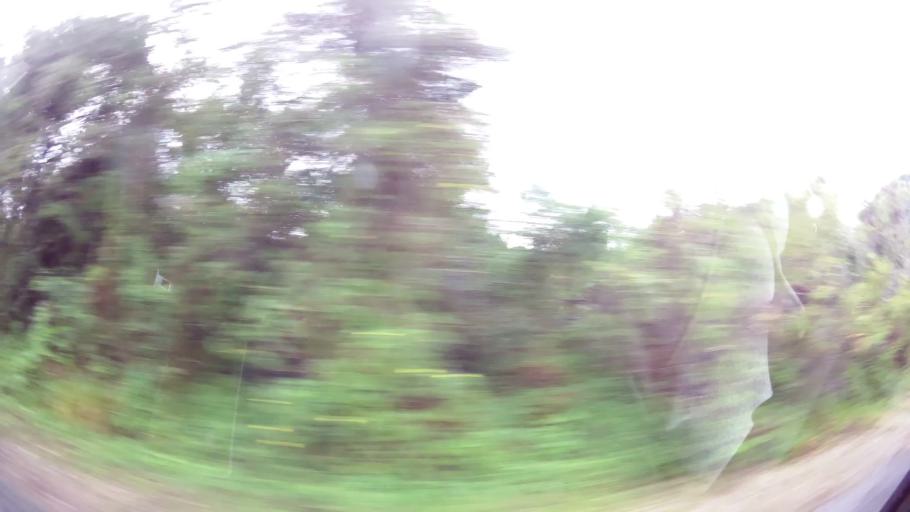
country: ZA
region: Eastern Cape
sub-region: Nelson Mandela Bay Metropolitan Municipality
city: Port Elizabeth
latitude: -34.0182
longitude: 25.5101
